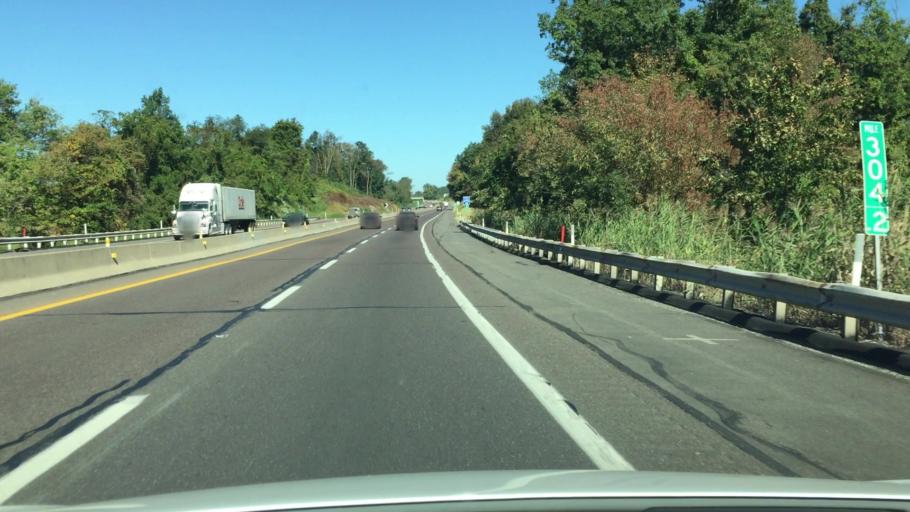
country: US
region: Pennsylvania
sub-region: Chester County
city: Elverson
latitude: 40.1267
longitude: -75.7864
